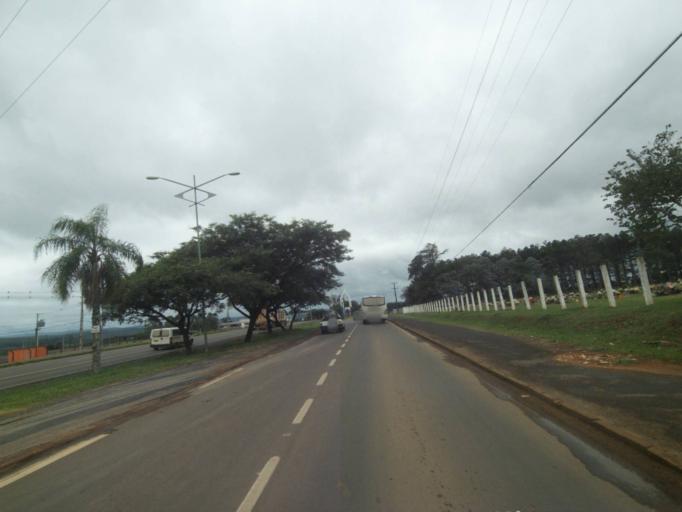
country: BR
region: Parana
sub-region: Telemaco Borba
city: Telemaco Borba
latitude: -24.3414
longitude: -50.6570
